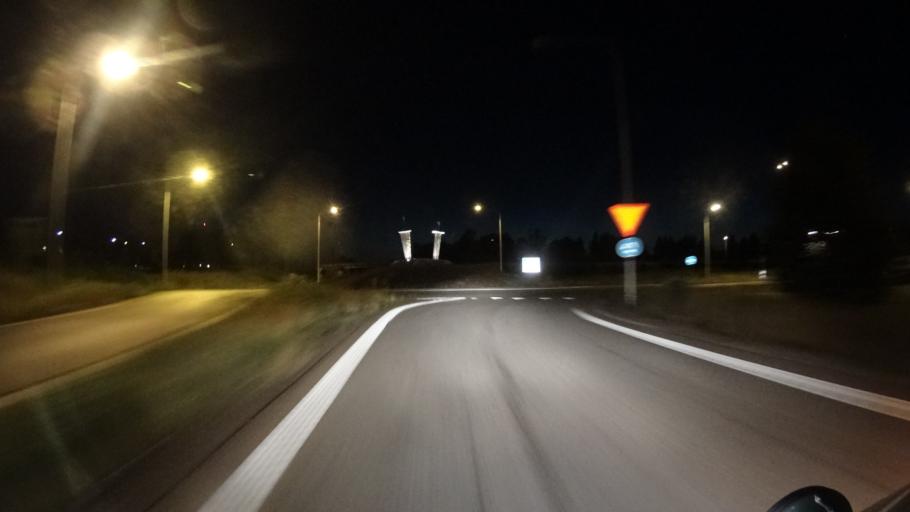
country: SE
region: OEstergoetland
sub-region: Odeshogs Kommun
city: OEdeshoeg
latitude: 58.2332
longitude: 14.6704
